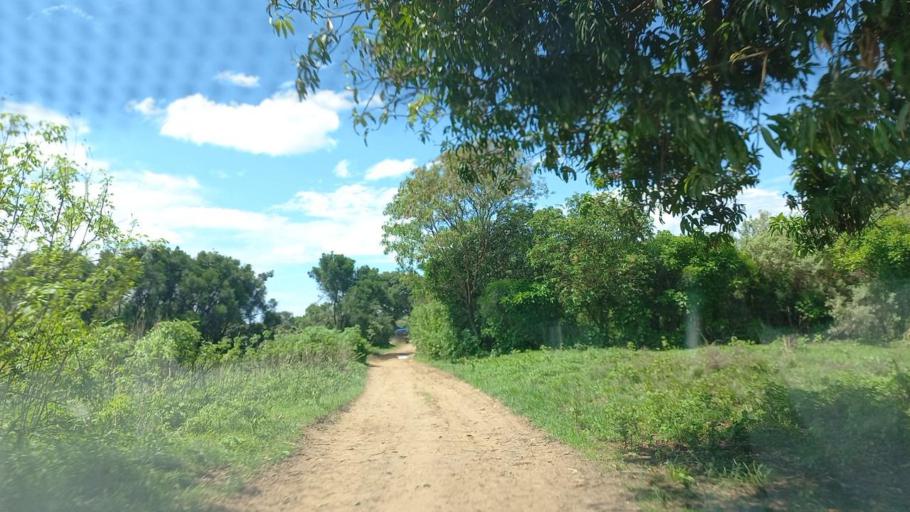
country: ZM
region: North-Western
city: Kabompo
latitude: -13.6176
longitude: 24.2097
